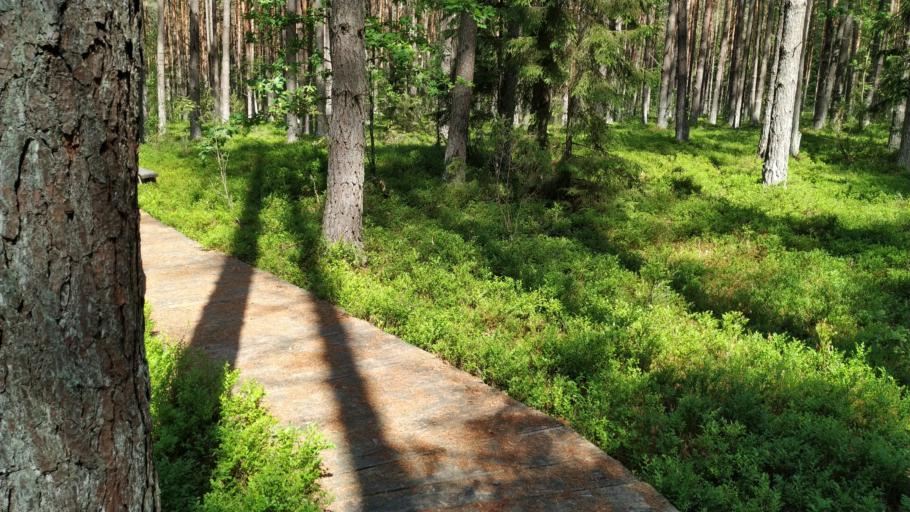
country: LT
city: Nemencine
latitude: 54.8091
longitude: 25.3975
